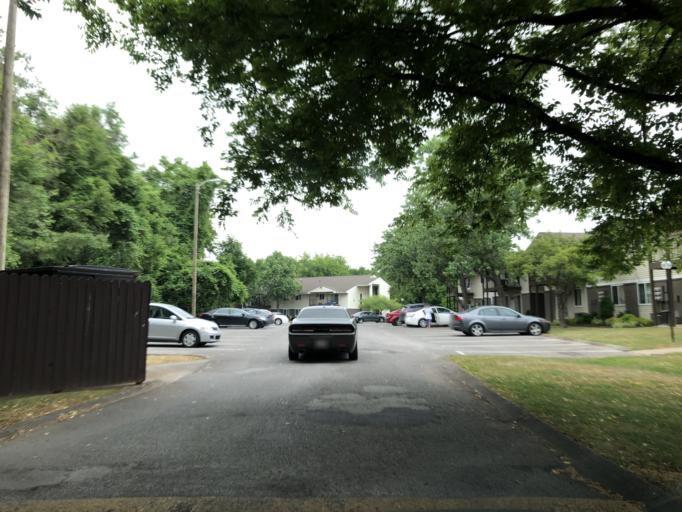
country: US
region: Tennessee
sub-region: Davidson County
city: Goodlettsville
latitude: 36.2848
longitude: -86.7211
